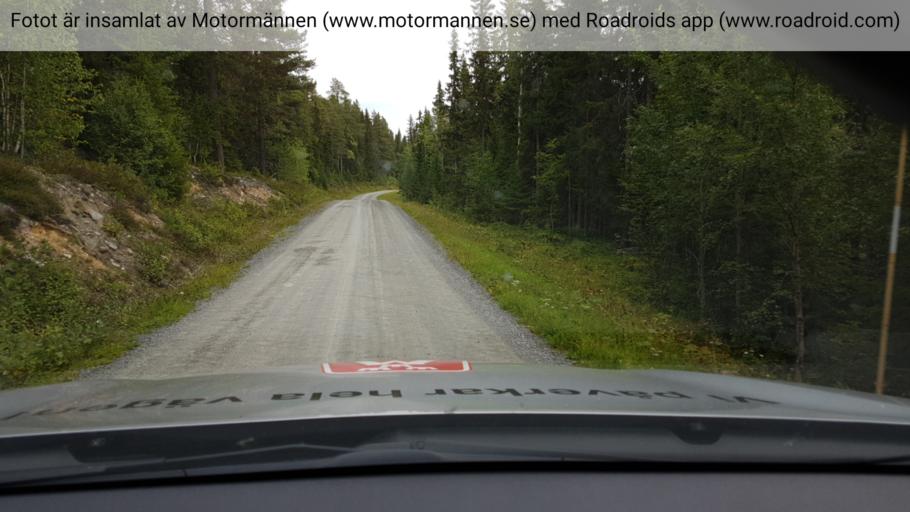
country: SE
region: Jaemtland
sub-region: Krokoms Kommun
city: Valla
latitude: 63.5833
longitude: 13.9693
